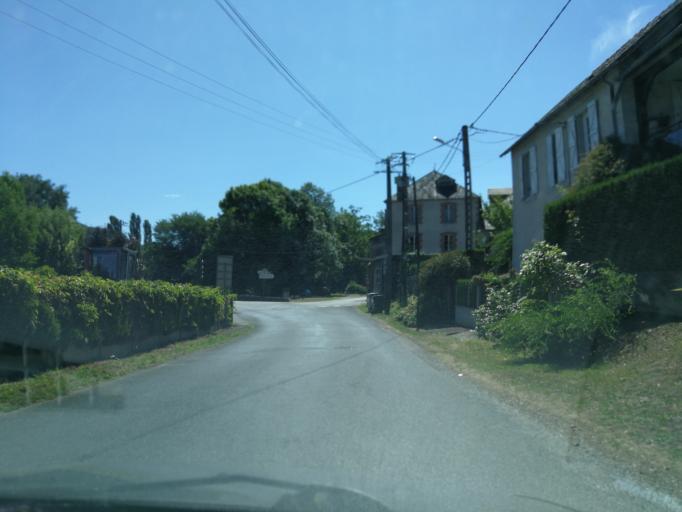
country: FR
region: Limousin
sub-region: Departement de la Correze
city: Argentat
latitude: 45.0938
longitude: 1.9238
